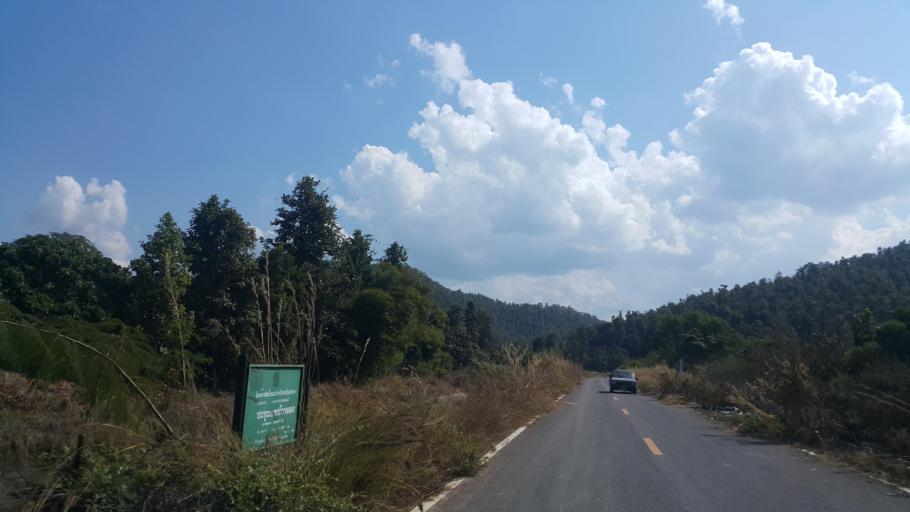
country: TH
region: Lamphun
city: Ban Thi
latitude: 18.6443
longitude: 99.1651
